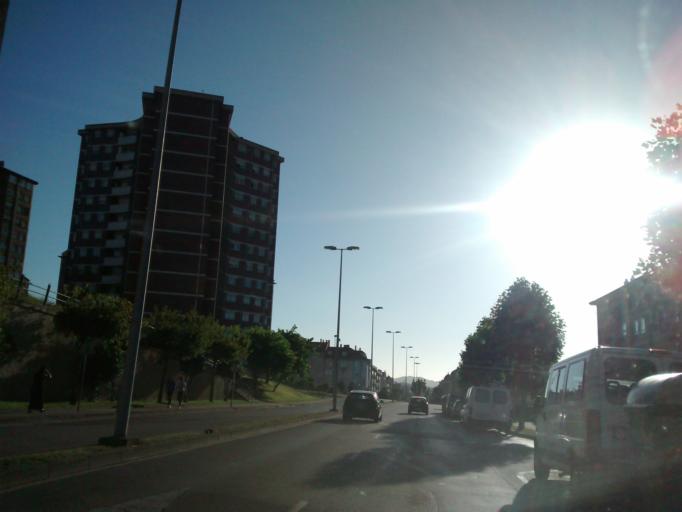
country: ES
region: Cantabria
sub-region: Provincia de Cantabria
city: Santander
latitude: 43.4594
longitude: -3.8467
